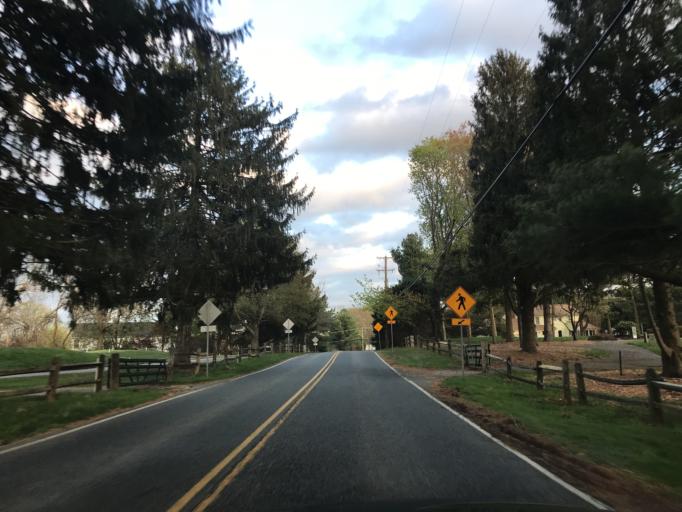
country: US
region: Maryland
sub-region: Harford County
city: Bel Air South
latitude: 39.5172
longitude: -76.2984
